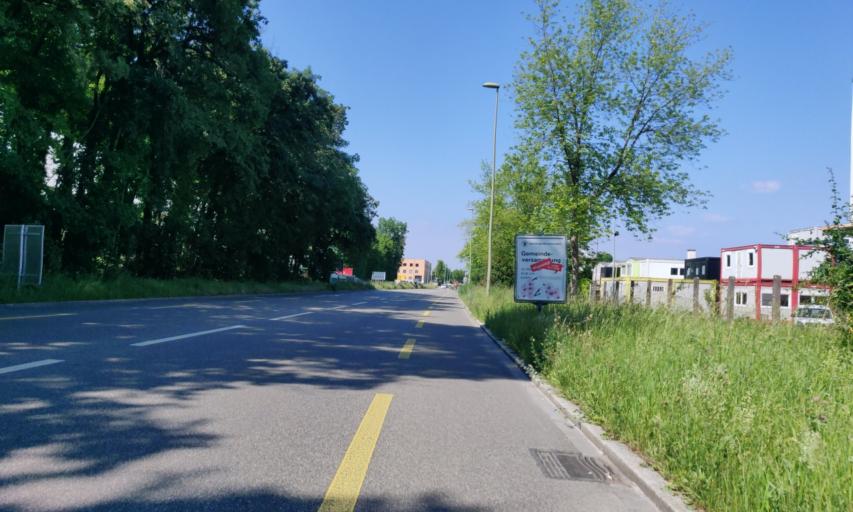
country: CH
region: Basel-Landschaft
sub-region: Bezirk Arlesheim
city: Munchenstein
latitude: 47.5223
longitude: 7.6035
